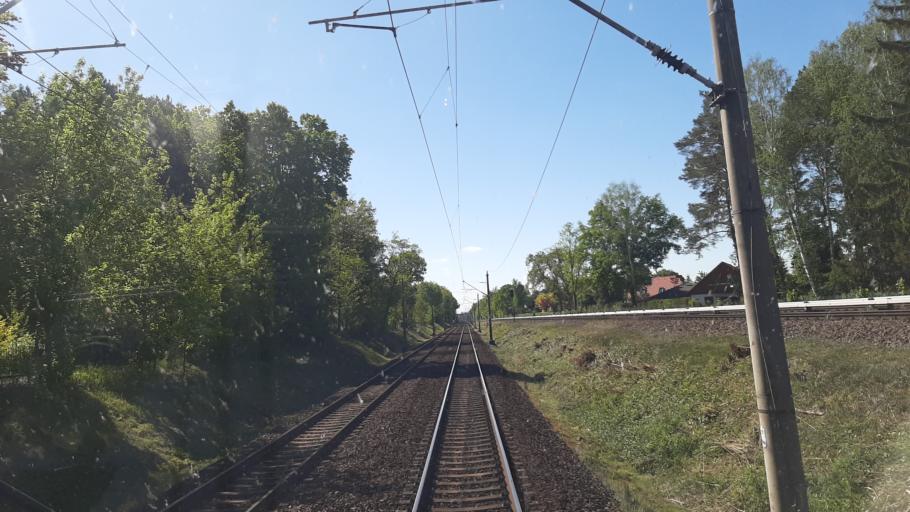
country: DE
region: Brandenburg
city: Birkenwerder
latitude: 52.7098
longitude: 13.2793
